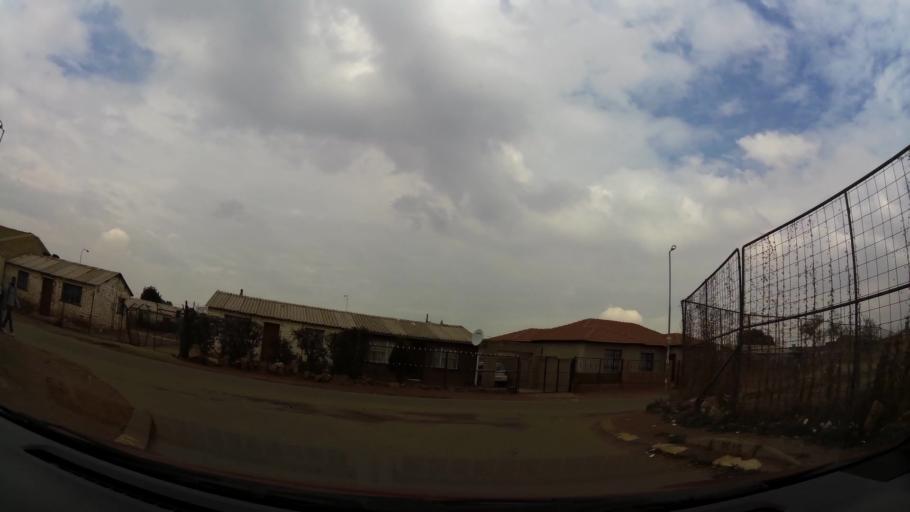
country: ZA
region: Gauteng
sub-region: City of Johannesburg Metropolitan Municipality
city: Soweto
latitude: -26.2561
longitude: 27.8266
